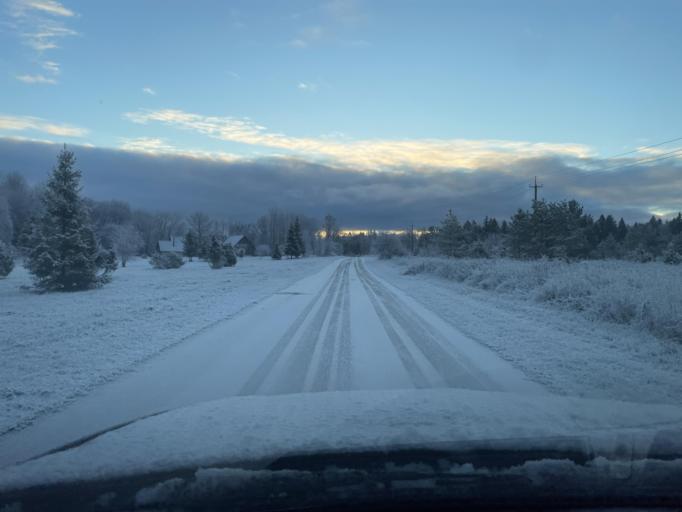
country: EE
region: Harju
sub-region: Keila linn
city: Keila
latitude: 59.3112
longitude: 24.2781
